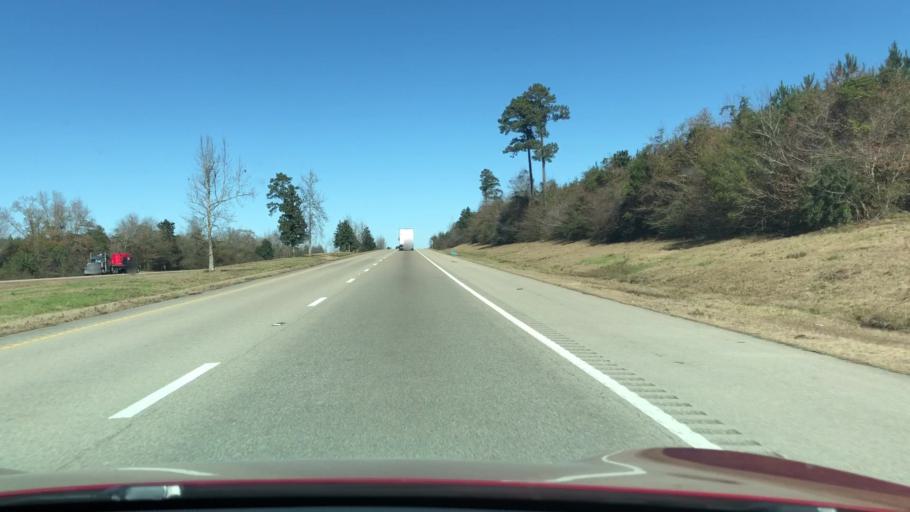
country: US
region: Mississippi
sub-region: Pearl River County
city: Poplarville
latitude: 30.7676
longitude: -89.5211
